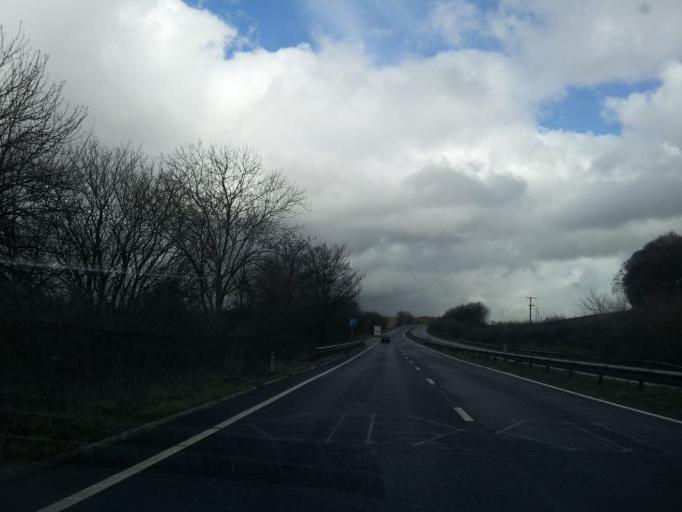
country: GB
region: England
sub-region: Somerset
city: Castle Cary
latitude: 51.0369
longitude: -2.5099
